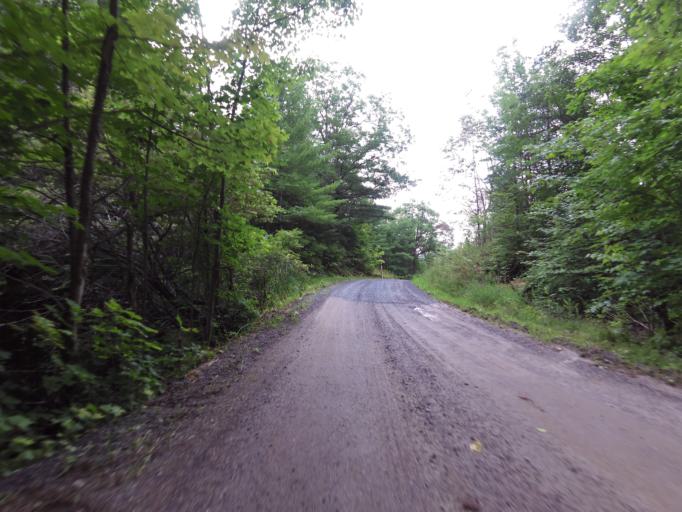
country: CA
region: Ontario
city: Kingston
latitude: 44.5645
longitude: -76.5795
